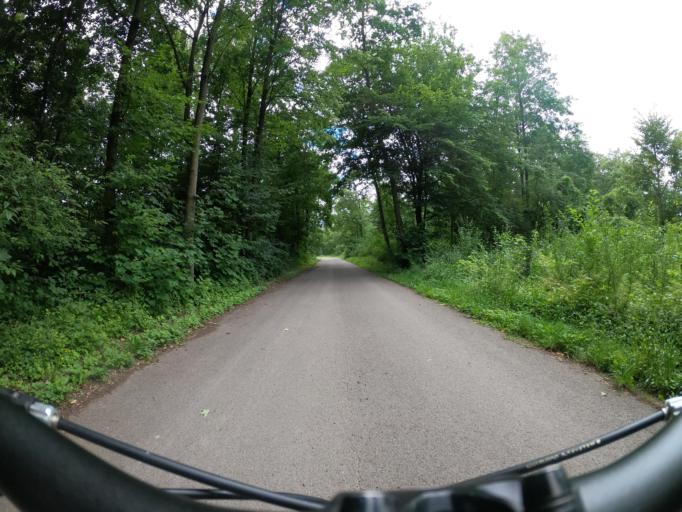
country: DE
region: Bavaria
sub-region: Swabia
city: Nersingen
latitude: 48.4377
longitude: 10.1065
